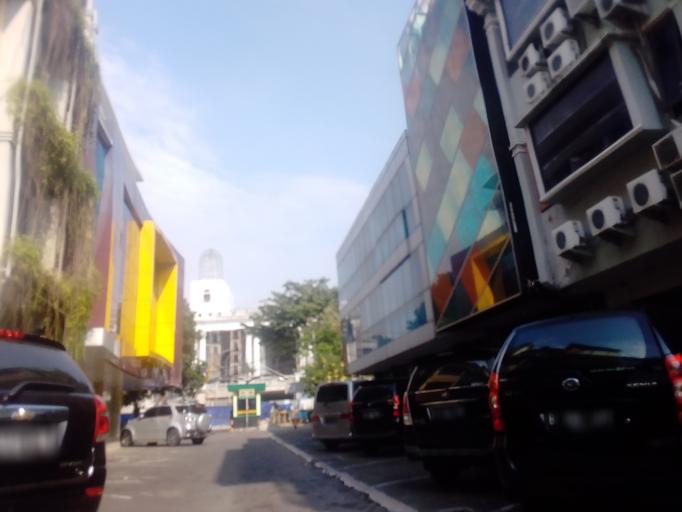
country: ID
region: Jakarta Raya
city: Jakarta
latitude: -6.2542
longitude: 106.7998
